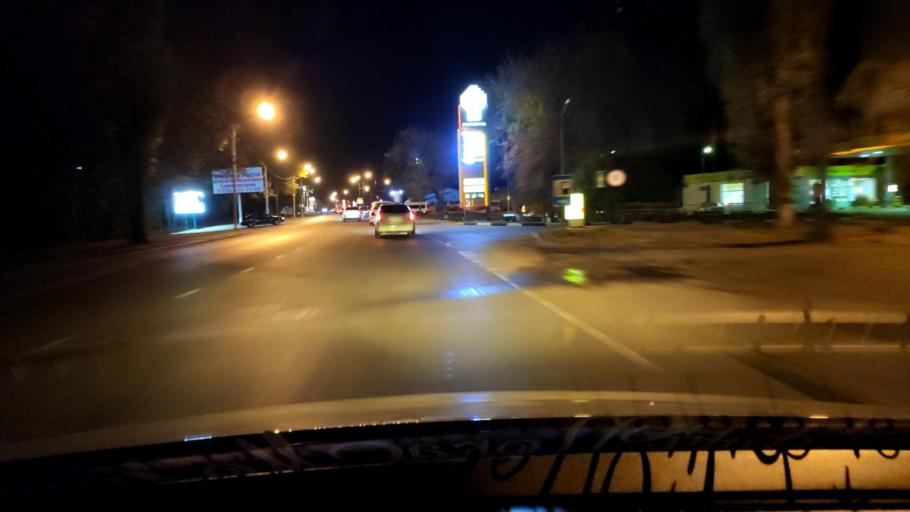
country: RU
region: Voronezj
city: Voronezh
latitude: 51.6204
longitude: 39.1761
